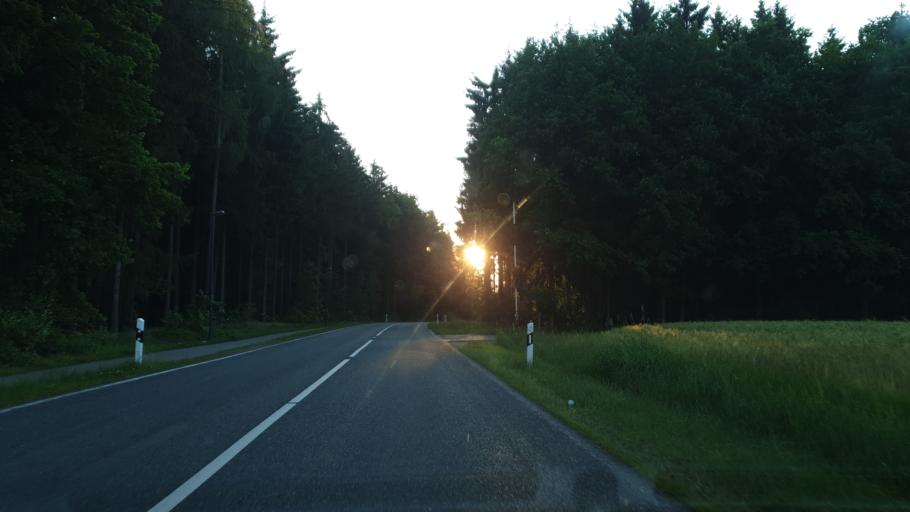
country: DE
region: Saxony
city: Oelsnitz
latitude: 50.7062
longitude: 12.7137
